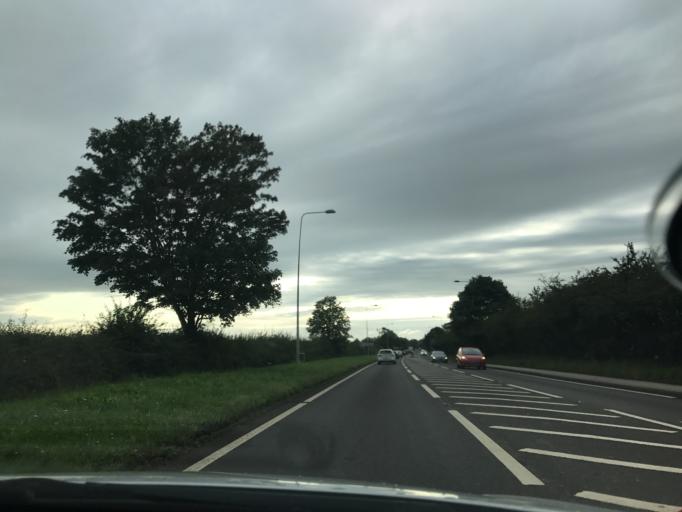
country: GB
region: England
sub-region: Cheshire West and Chester
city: Guilden Sutton
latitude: 53.1988
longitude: -2.8093
